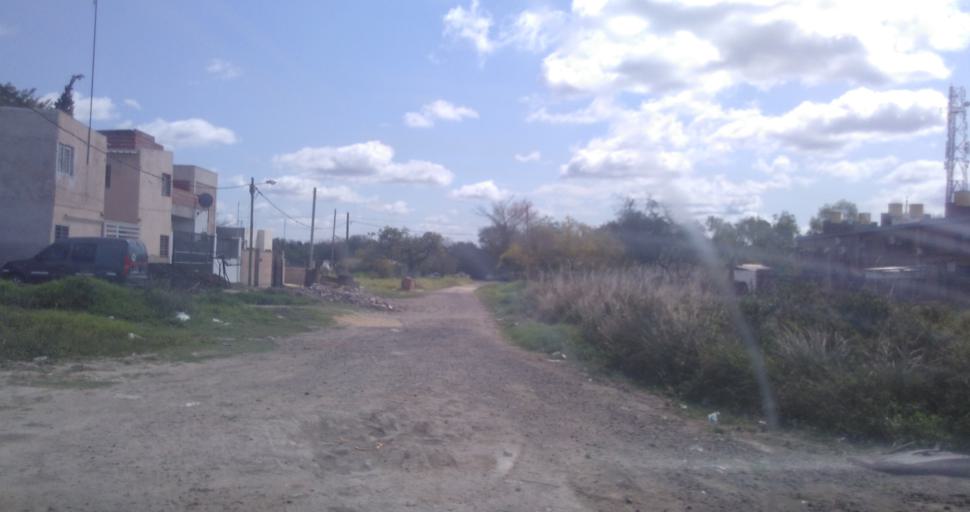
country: AR
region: Chaco
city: Fontana
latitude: -27.4277
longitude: -59.0307
